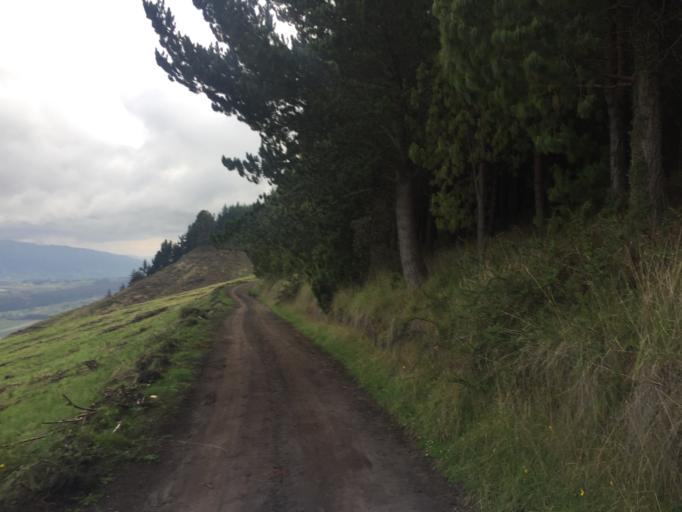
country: EC
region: Imbabura
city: Ibarra
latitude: 0.2277
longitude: -78.1232
